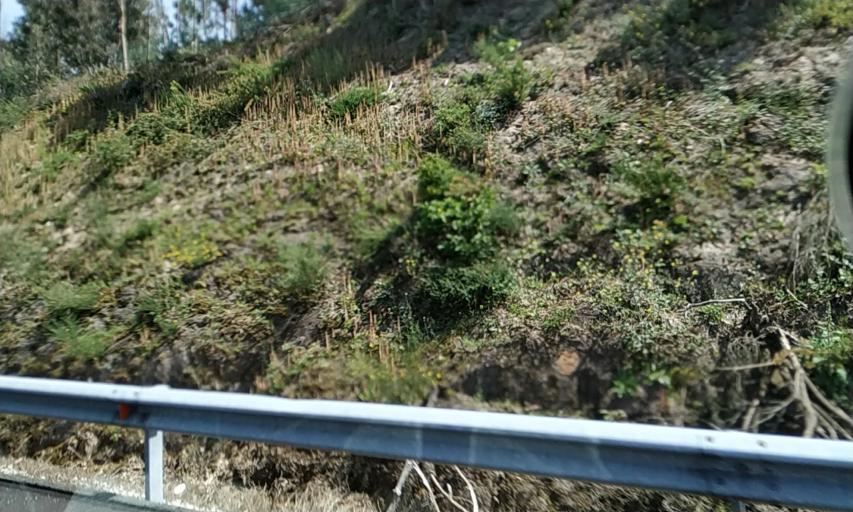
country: ES
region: Galicia
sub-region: Provincia de Pontevedra
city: Valga
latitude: 42.6825
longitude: -8.6342
